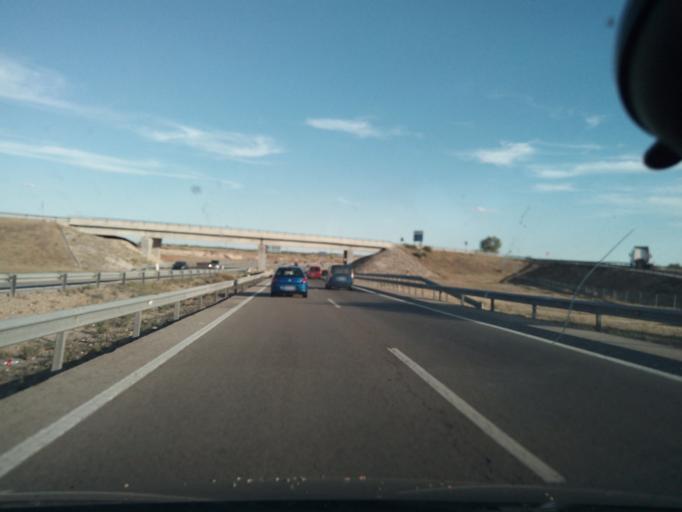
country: ES
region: Castille-La Mancha
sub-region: Province of Toledo
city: Dosbarrios
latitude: 39.8905
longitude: -3.4723
